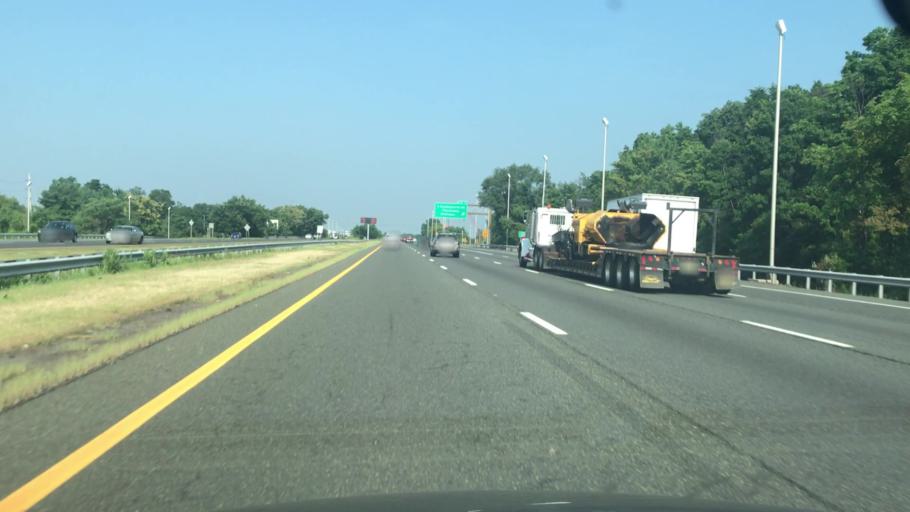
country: US
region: New Jersey
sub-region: Middlesex County
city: Society Hill
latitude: 40.5565
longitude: -74.4579
